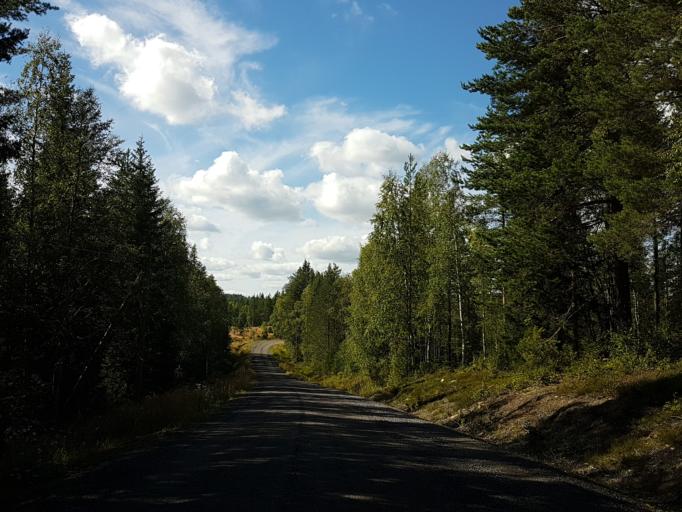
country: SE
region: Vaesterbotten
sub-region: Skelleftea Kommun
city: Burtraesk
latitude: 64.2791
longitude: 20.4750
